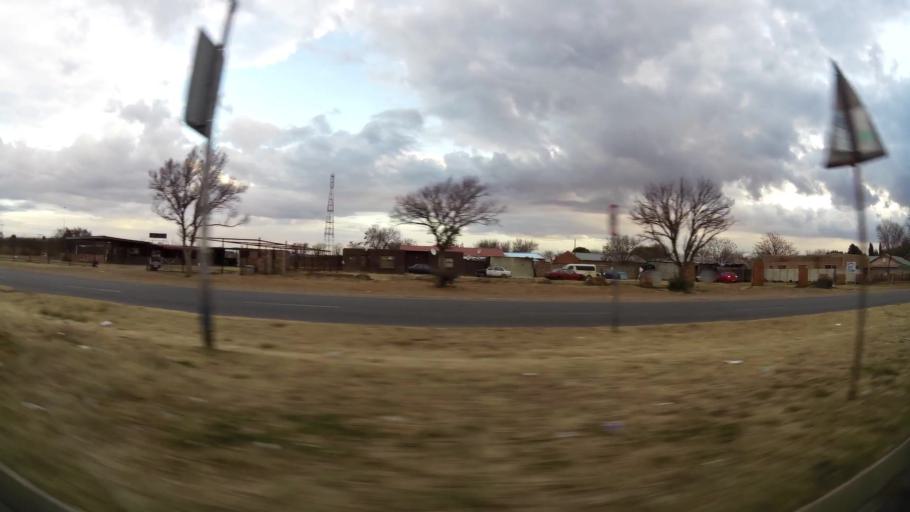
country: ZA
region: Orange Free State
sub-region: Lejweleputswa District Municipality
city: Welkom
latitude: -27.9752
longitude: 26.7725
